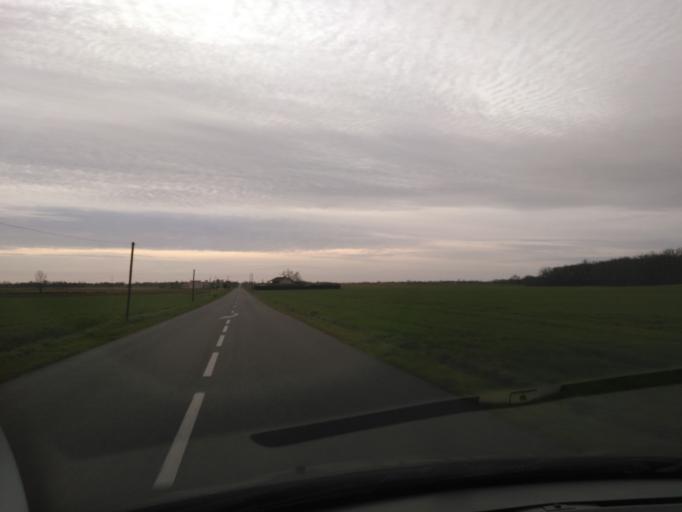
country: FR
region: Midi-Pyrenees
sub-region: Departement du Tarn-et-Garonne
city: Verdun-sur-Garonne
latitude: 43.8325
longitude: 1.1626
